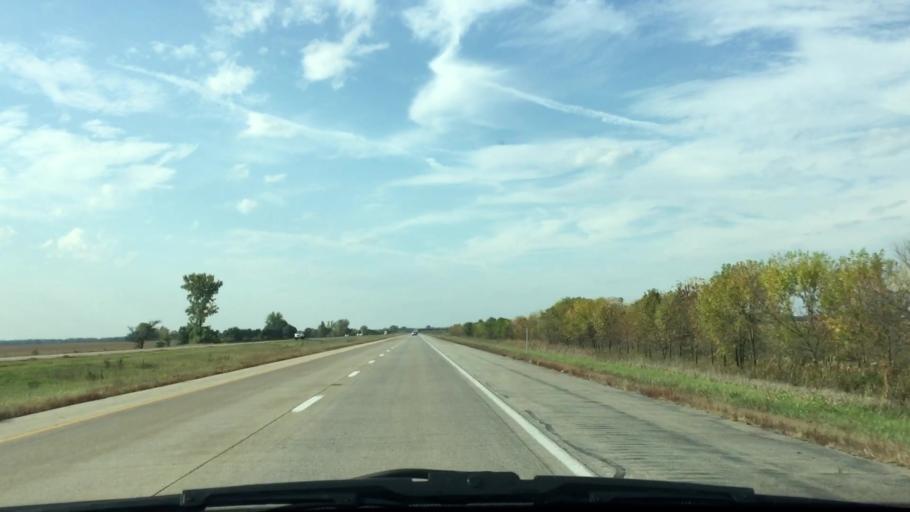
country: US
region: Illinois
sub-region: Whiteside County
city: Erie
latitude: 41.6585
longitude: -90.1478
